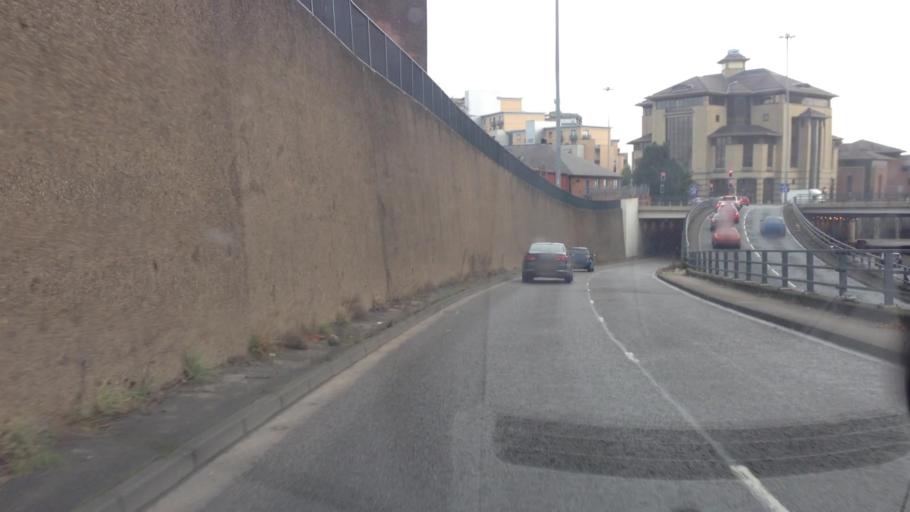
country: GB
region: England
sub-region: City and Borough of Leeds
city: Leeds
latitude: 53.8054
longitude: -1.5449
